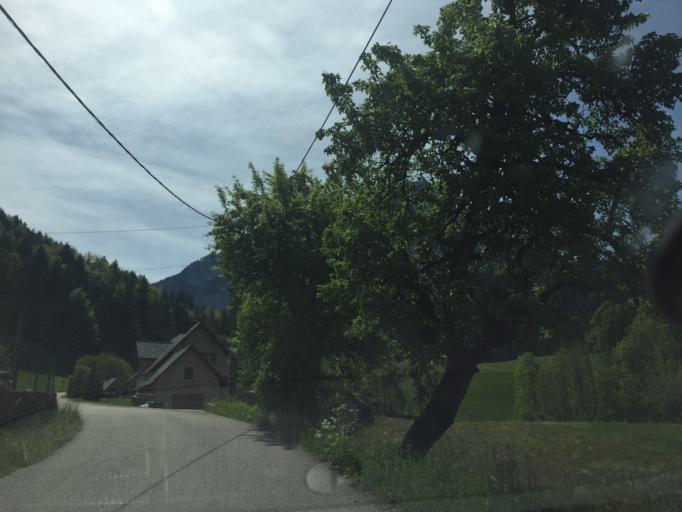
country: FR
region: Rhone-Alpes
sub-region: Departement de l'Isere
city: Barraux
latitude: 45.4492
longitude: 5.8935
